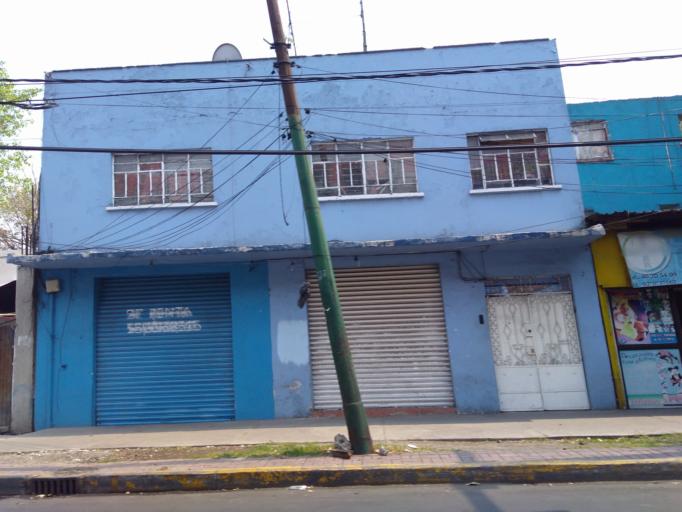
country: MX
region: Mexico City
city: Mexico City
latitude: 19.4346
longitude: -99.1187
